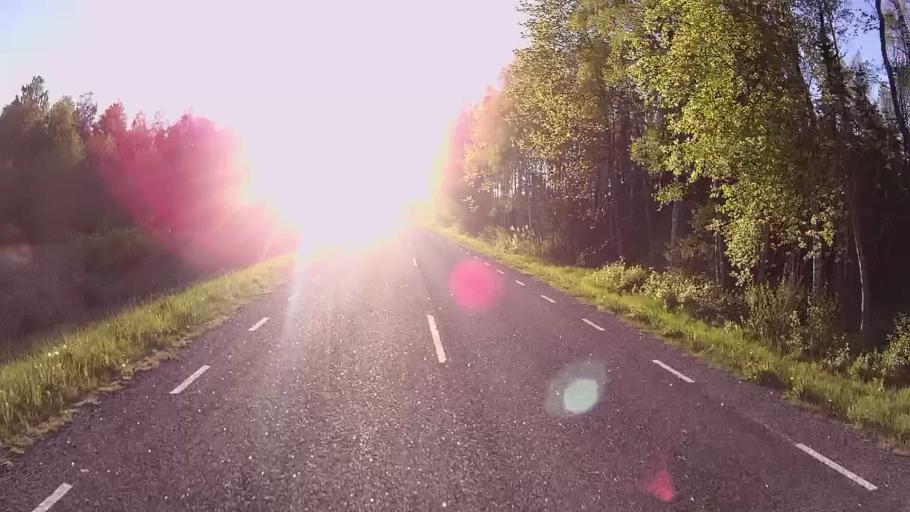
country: EE
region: Jogevamaa
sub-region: Poltsamaa linn
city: Poltsamaa
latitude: 58.5229
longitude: 25.9667
